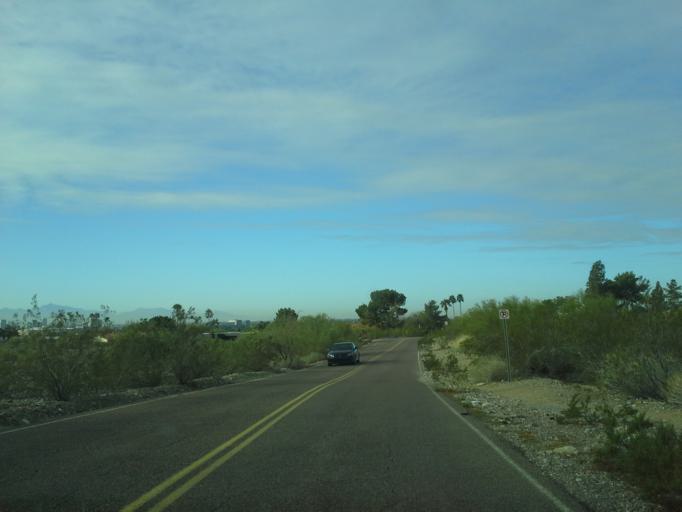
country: US
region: Arizona
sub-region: Maricopa County
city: Paradise Valley
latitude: 33.5372
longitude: -112.0265
